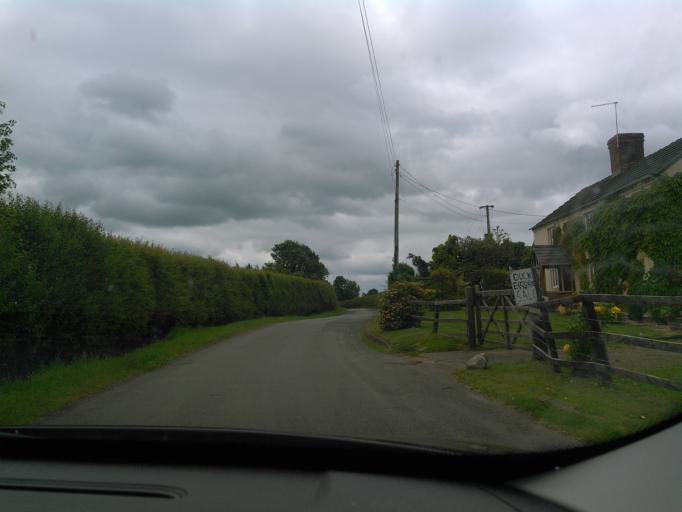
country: GB
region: England
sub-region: Shropshire
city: Wem
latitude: 52.9155
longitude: -2.7285
